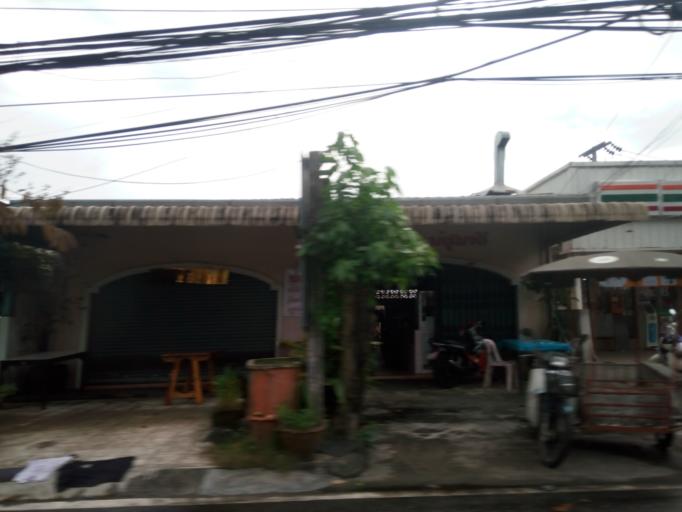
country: TH
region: Phuket
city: Thalang
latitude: 7.9822
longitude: 98.3625
